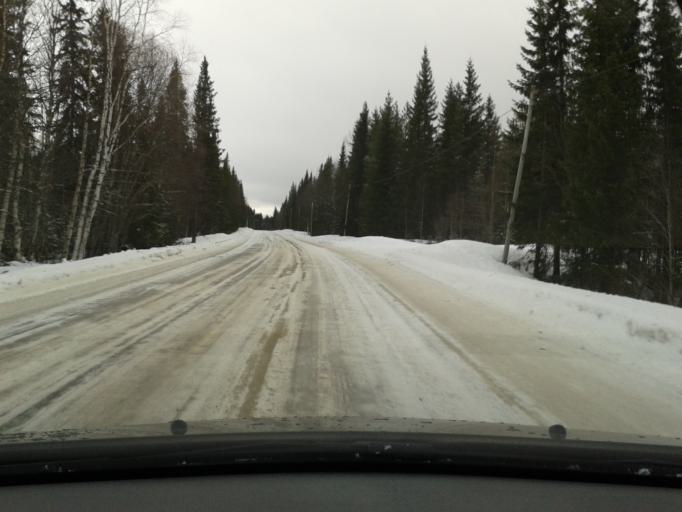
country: SE
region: Vaesterbotten
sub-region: Vilhelmina Kommun
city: Sjoberg
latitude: 64.6725
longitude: 16.2941
